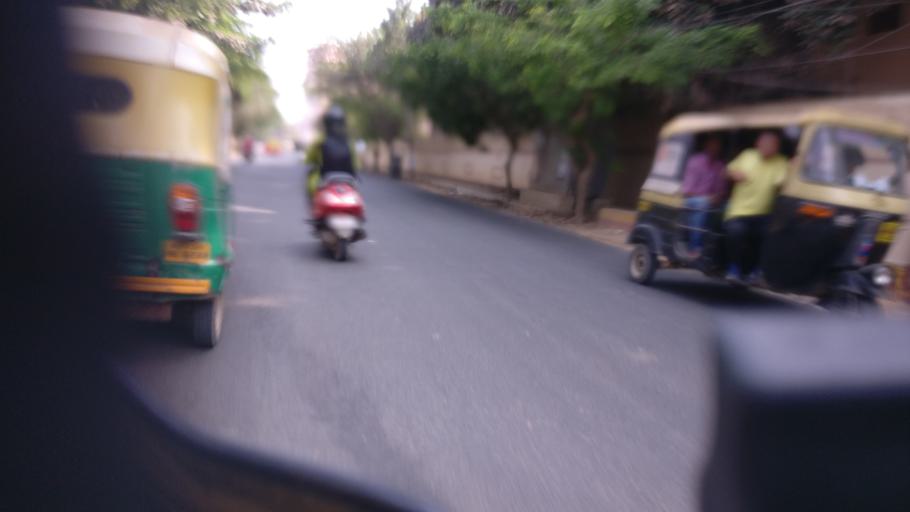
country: IN
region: Karnataka
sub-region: Bangalore Urban
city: Bangalore
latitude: 12.8957
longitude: 77.6748
